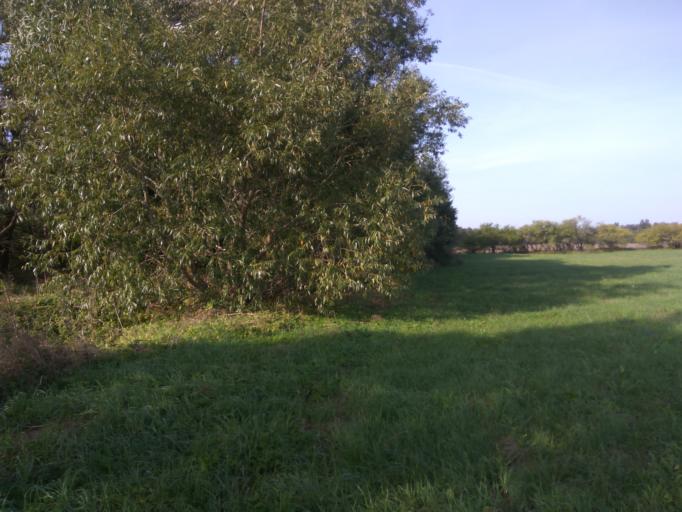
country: LV
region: Ventspils
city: Ventspils
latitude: 57.3546
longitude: 21.6411
